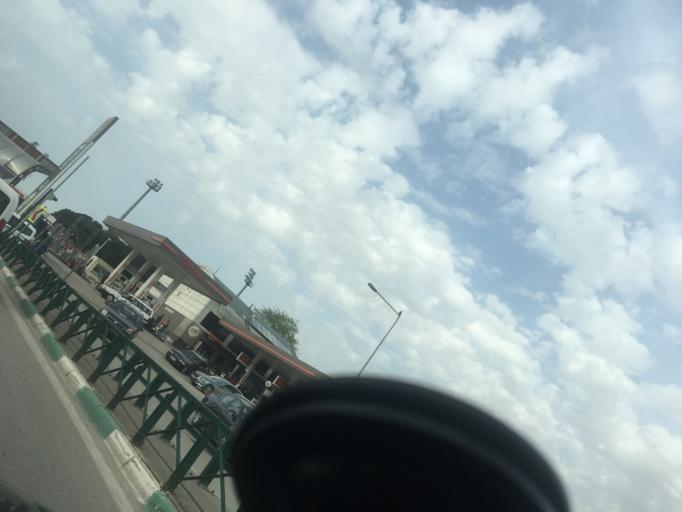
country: TR
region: Bursa
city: Yildirim
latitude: 40.1989
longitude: 29.0459
